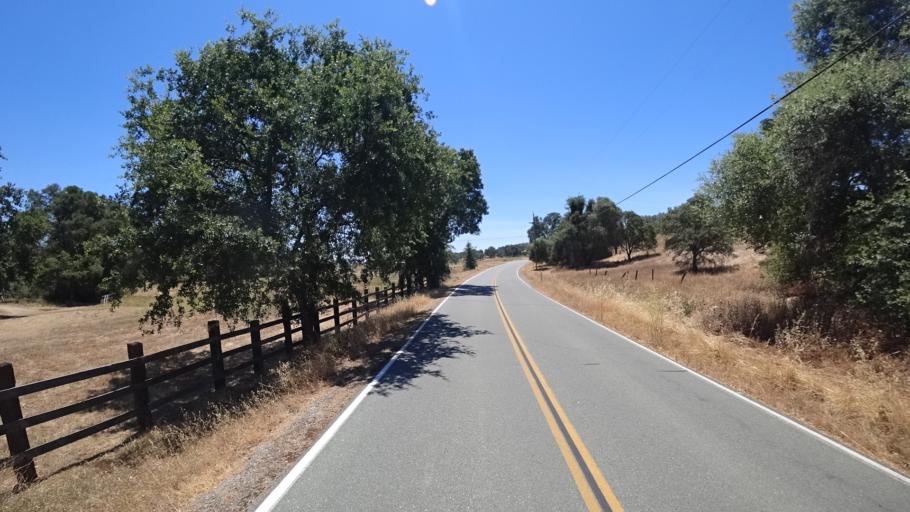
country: US
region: California
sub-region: Calaveras County
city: Valley Springs
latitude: 38.2077
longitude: -120.8252
